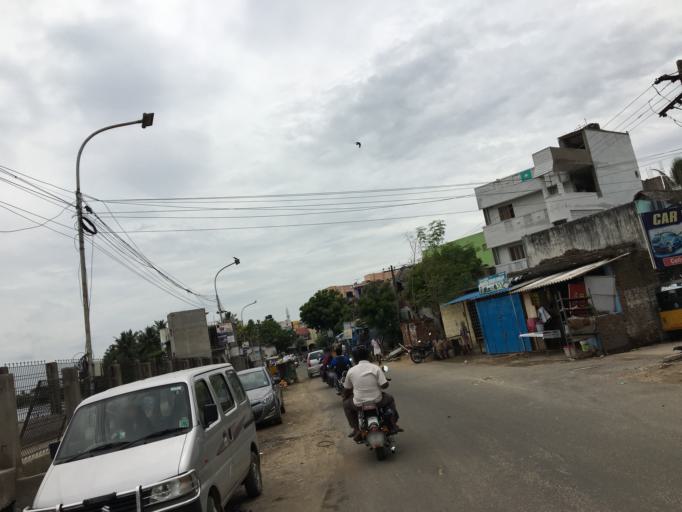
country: IN
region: Tamil Nadu
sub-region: Kancheepuram
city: Alandur
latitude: 12.9885
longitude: 80.2158
